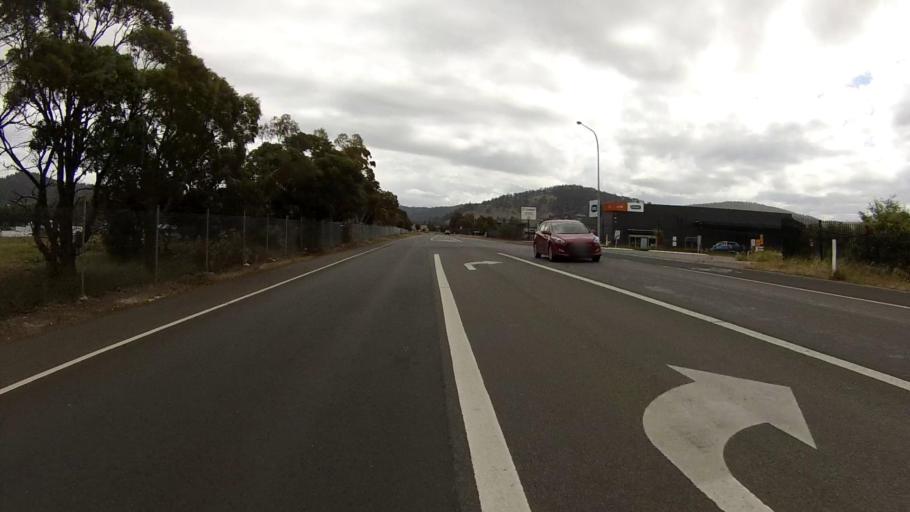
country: AU
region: Tasmania
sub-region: Clarence
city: Cambridge
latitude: -42.8303
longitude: 147.4702
